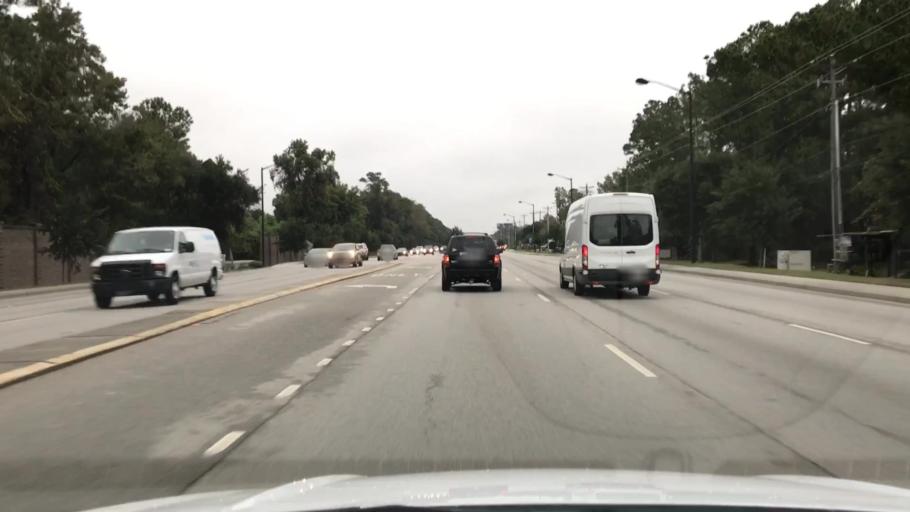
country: US
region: South Carolina
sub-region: Charleston County
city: Isle of Palms
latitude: 32.8379
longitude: -79.8212
